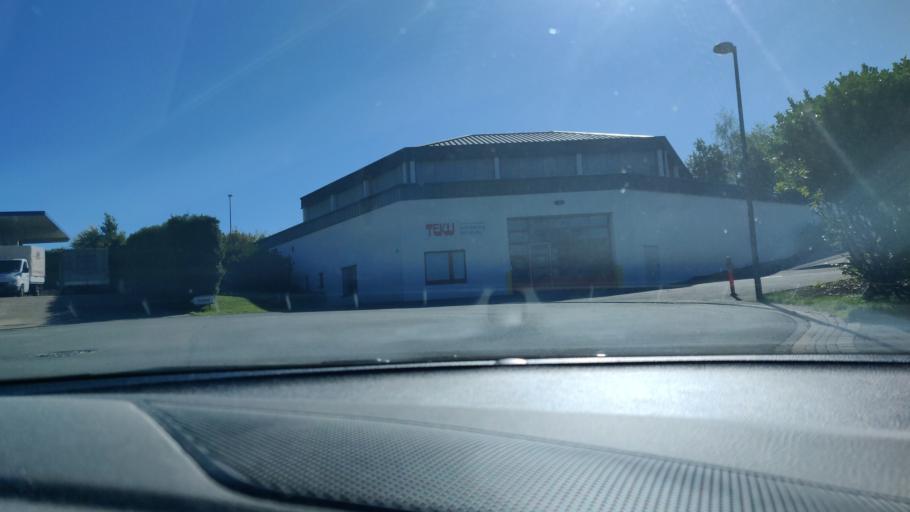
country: DE
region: North Rhine-Westphalia
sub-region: Regierungsbezirk Dusseldorf
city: Velbert
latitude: 51.3513
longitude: 7.0808
